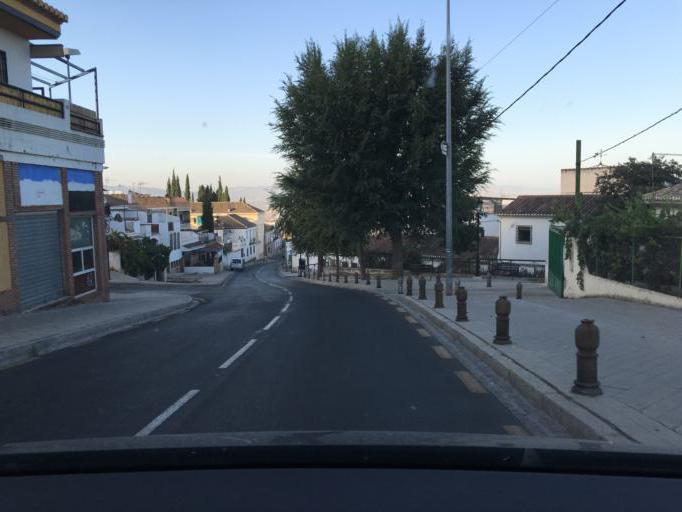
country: ES
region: Andalusia
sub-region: Provincia de Granada
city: Granada
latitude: 37.1888
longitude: -3.5900
